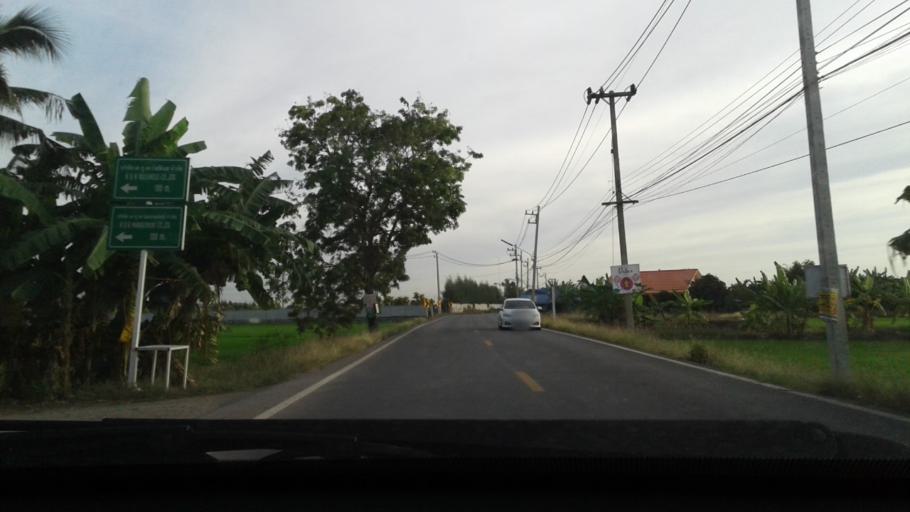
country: TH
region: Nonthaburi
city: Sai Noi
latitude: 13.9149
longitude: 100.2559
